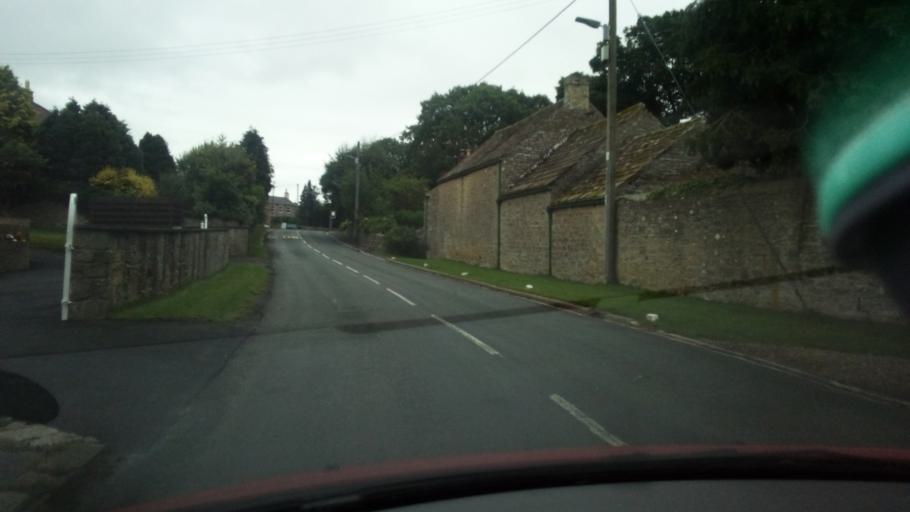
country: GB
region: England
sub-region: County Durham
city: Muggleswick
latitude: 54.8442
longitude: -1.9766
